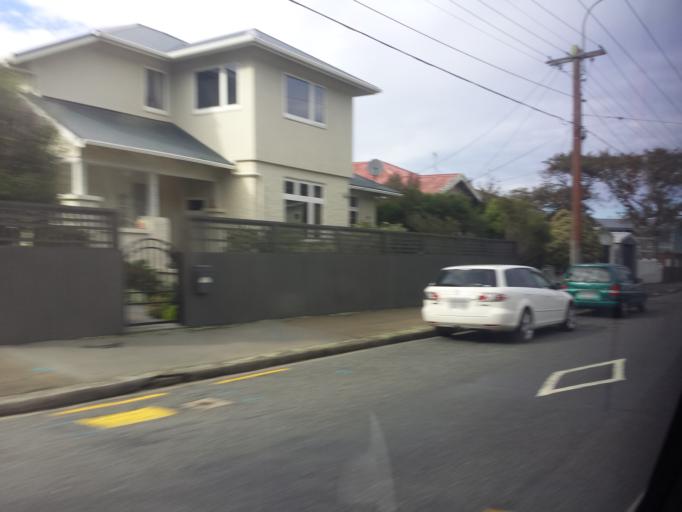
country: NZ
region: Wellington
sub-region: Wellington City
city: Wellington
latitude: -41.3076
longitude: 174.7929
